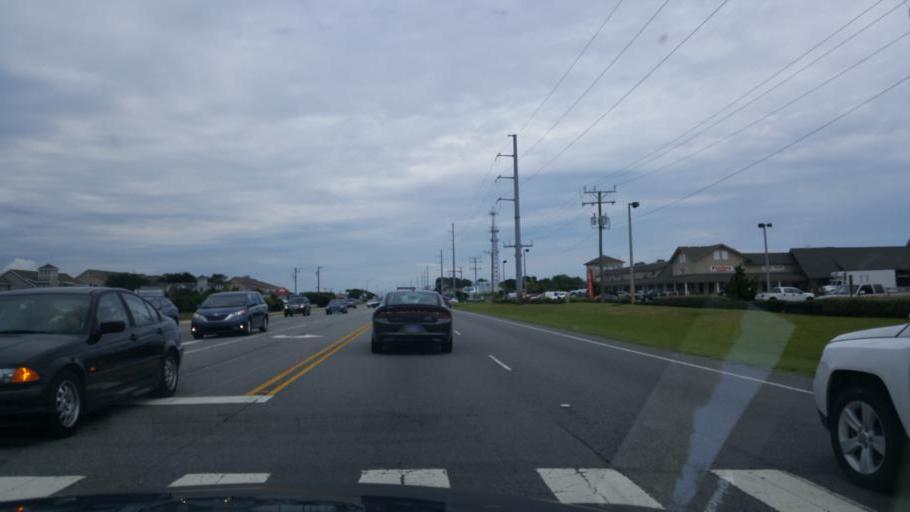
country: US
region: North Carolina
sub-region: Dare County
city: Nags Head
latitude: 35.9839
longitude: -75.6438
